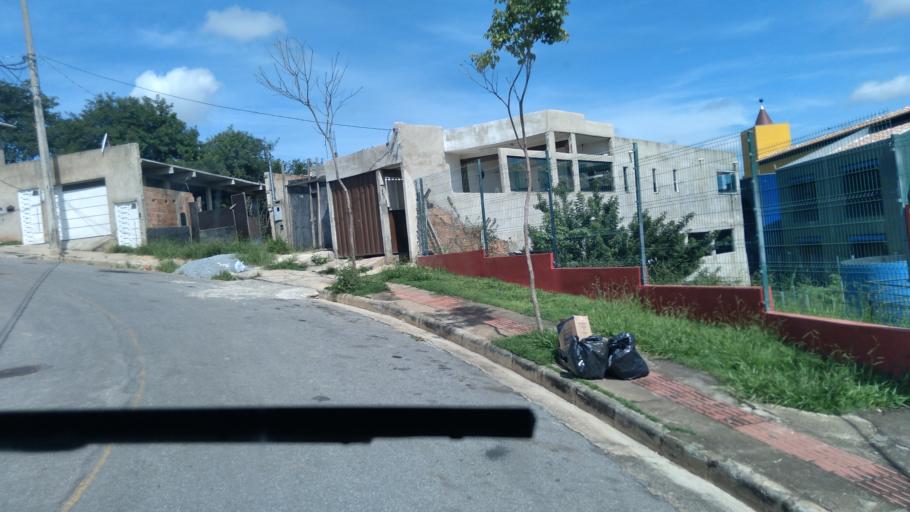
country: BR
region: Minas Gerais
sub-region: Santa Luzia
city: Santa Luzia
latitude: -19.8406
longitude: -43.8803
